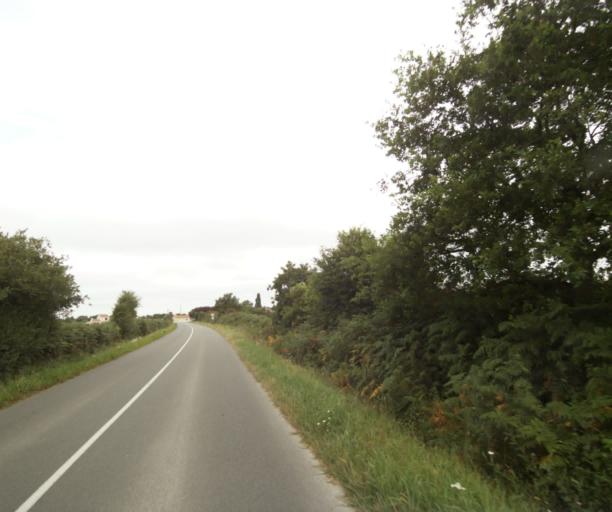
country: FR
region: Pays de la Loire
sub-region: Departement de la Vendee
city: Sainte-Foy
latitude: 46.5123
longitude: -1.6864
